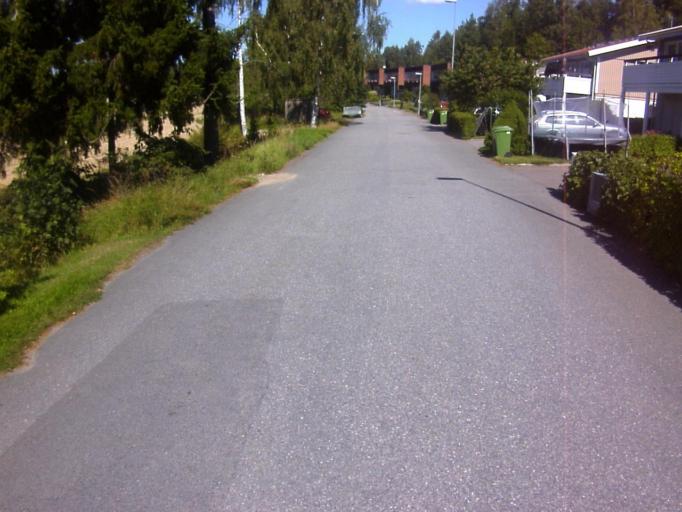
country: SE
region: Soedermanland
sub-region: Eskilstuna Kommun
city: Hallbybrunn
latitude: 59.3841
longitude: 16.4292
